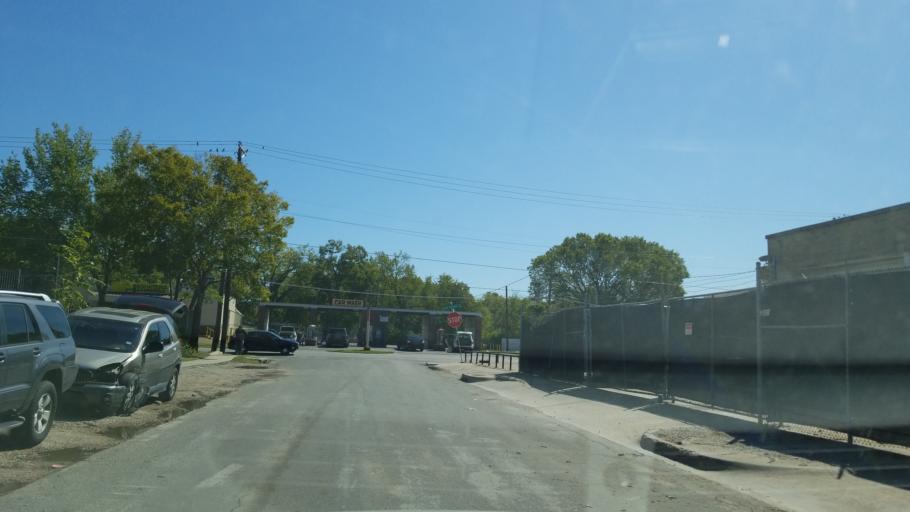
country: US
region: Texas
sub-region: Dallas County
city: Dallas
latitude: 32.7864
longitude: -96.7563
